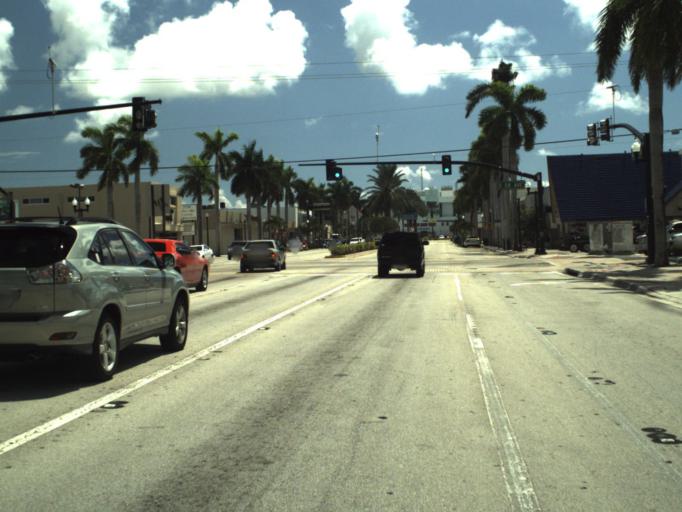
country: US
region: Florida
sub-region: Broward County
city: Hollywood
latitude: 26.0109
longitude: -80.1638
